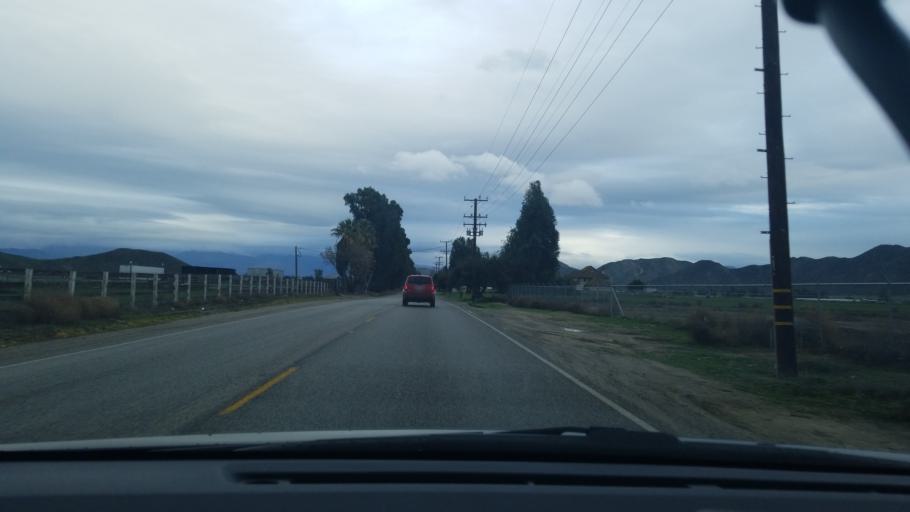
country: US
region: California
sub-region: Riverside County
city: Winchester
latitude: 33.7073
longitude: -117.0685
